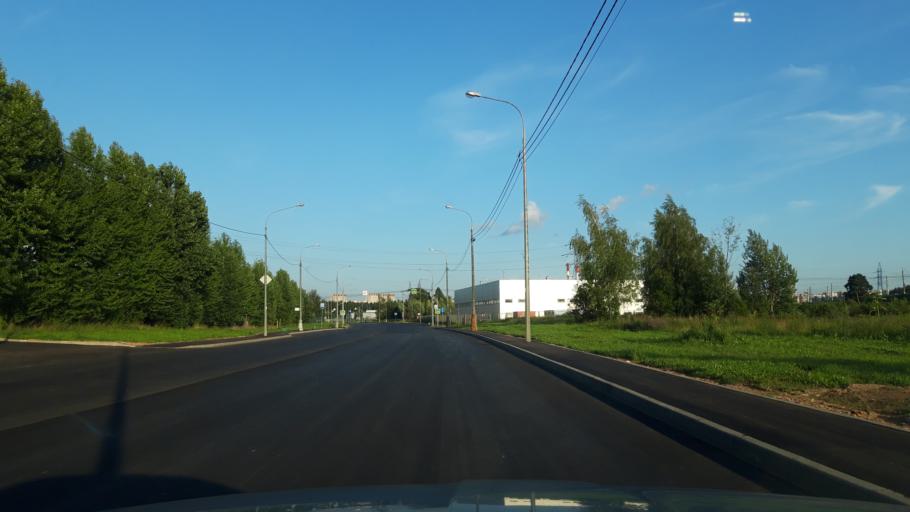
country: RU
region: Moskovskaya
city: Alabushevo
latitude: 56.0036
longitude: 37.1480
